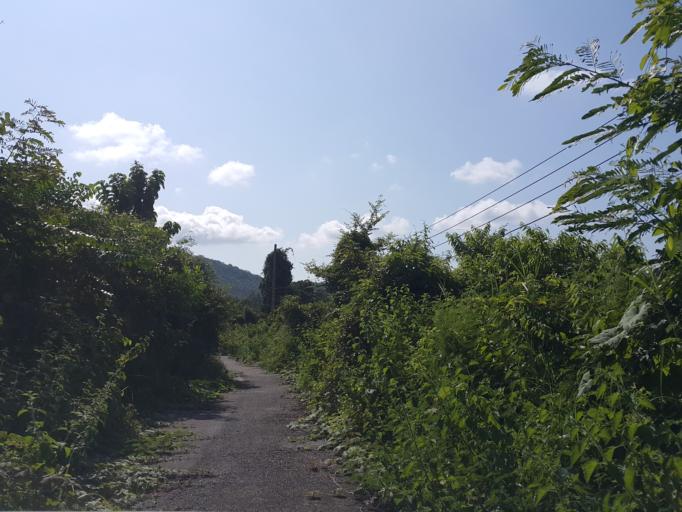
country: TH
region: Chiang Mai
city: Mae On
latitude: 18.8026
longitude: 99.1879
